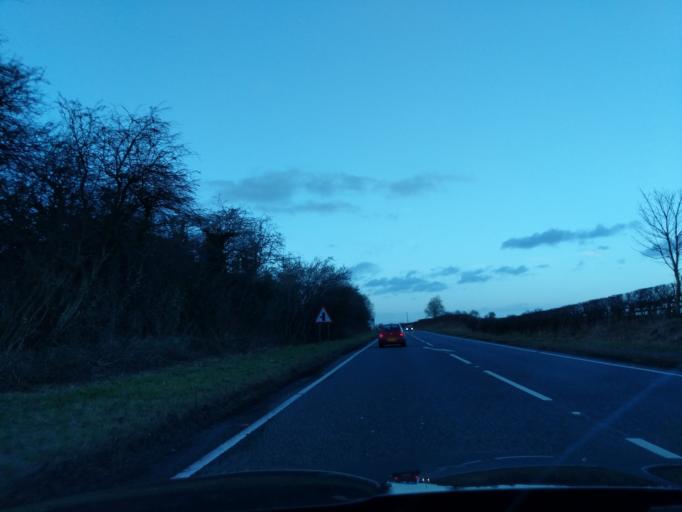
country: GB
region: England
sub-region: Northumberland
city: Felton
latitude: 55.2456
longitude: -1.7031
